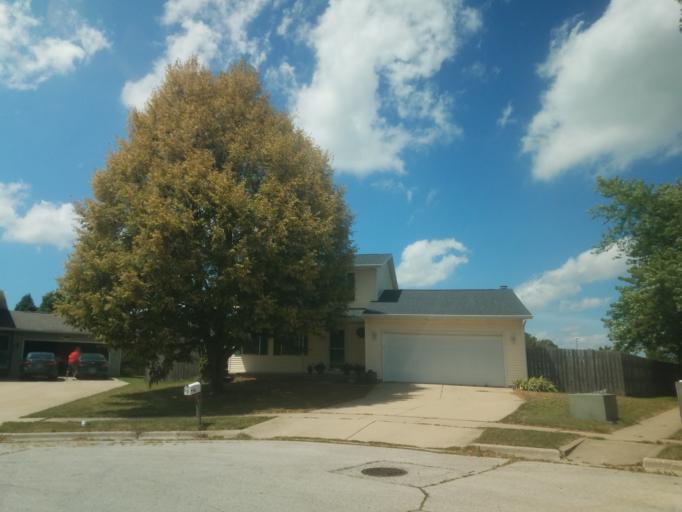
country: US
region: Illinois
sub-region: McLean County
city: Bloomington
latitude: 40.4453
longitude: -89.0290
